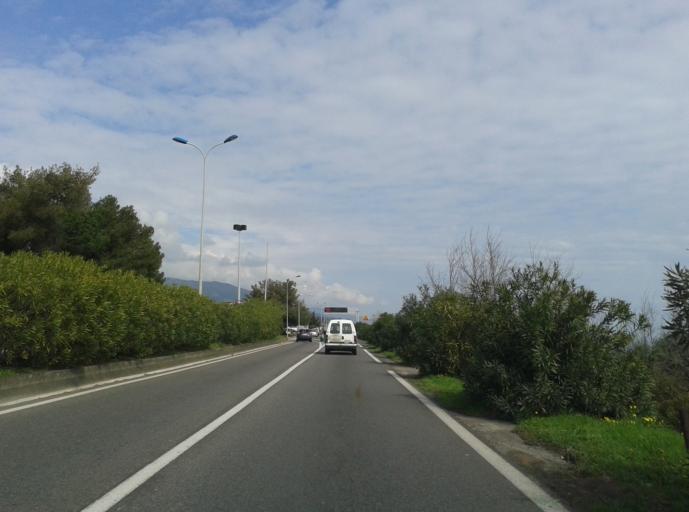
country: FR
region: Corsica
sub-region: Departement de la Haute-Corse
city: Furiani
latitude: 42.6700
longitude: 9.4434
